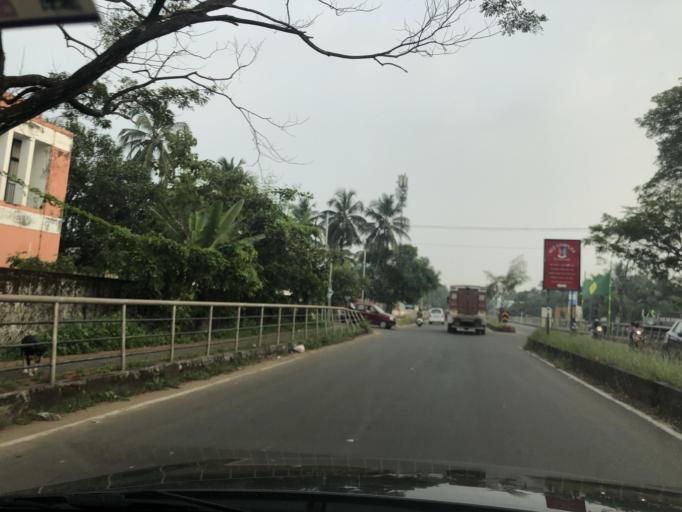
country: IN
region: Kerala
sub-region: Kozhikode
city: Kozhikode
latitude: 11.2845
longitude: 75.7608
